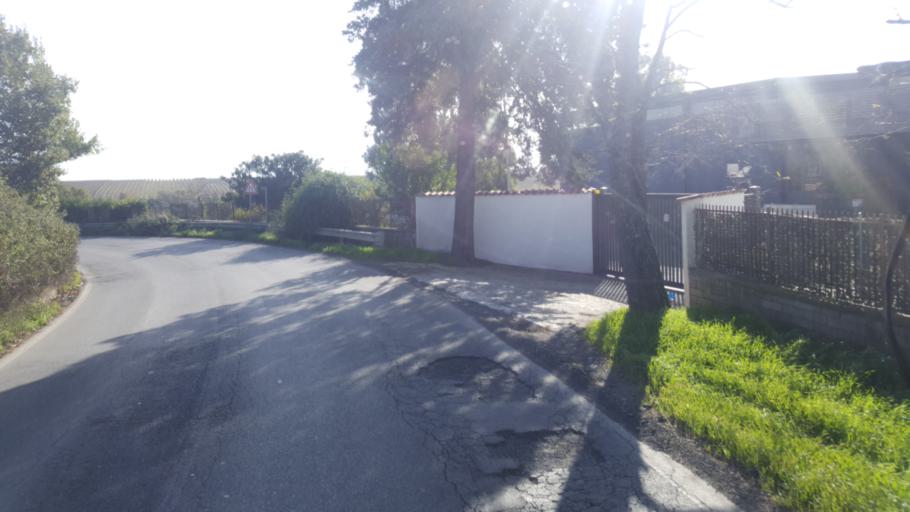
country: IT
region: Latium
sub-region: Citta metropolitana di Roma Capitale
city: Mantiglia di Ardea
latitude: 41.6895
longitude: 12.6006
